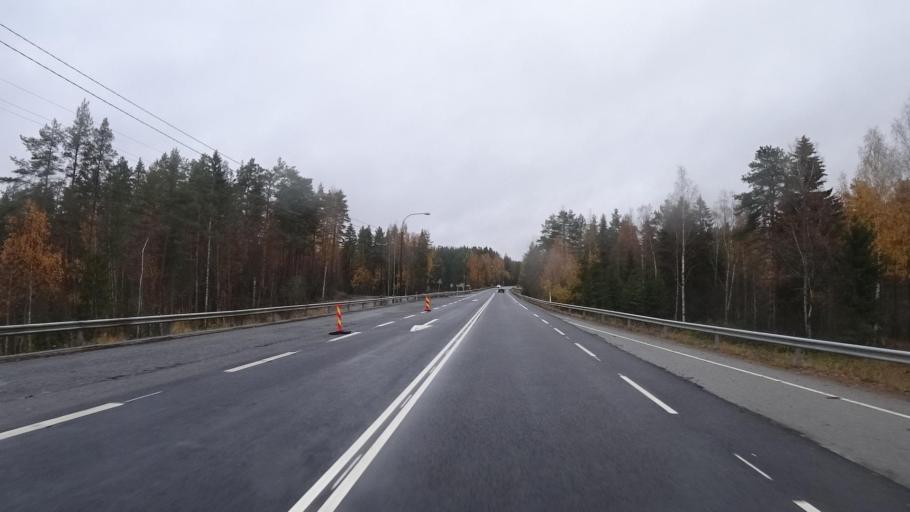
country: FI
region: Northern Savo
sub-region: Varkaus
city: Varkaus
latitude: 62.3197
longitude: 28.0043
